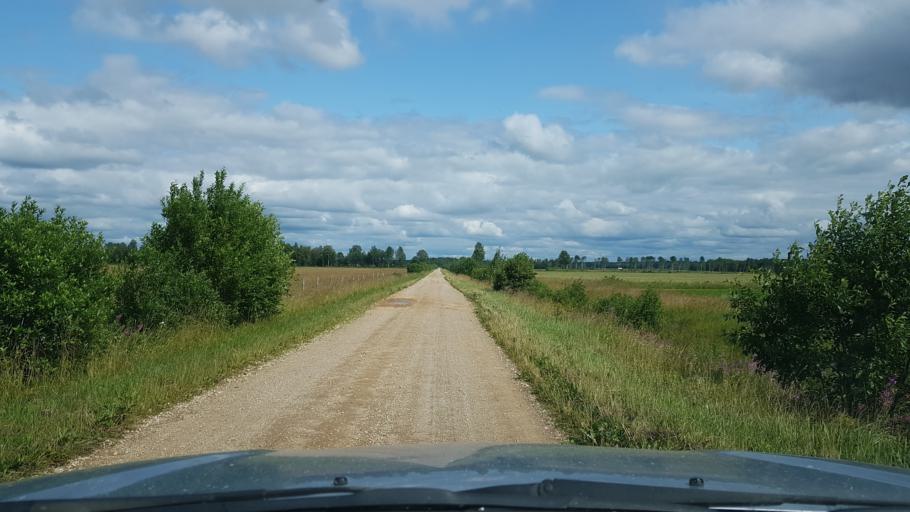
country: EE
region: Ida-Virumaa
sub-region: Sillamaee linn
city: Sillamae
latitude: 59.3703
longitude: 27.9014
